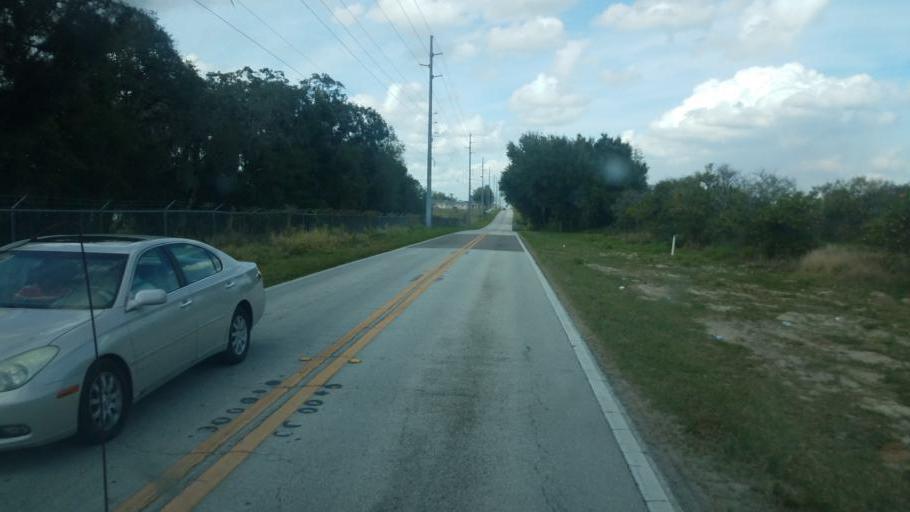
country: US
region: Florida
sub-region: Polk County
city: Haines City
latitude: 28.1152
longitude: -81.5904
